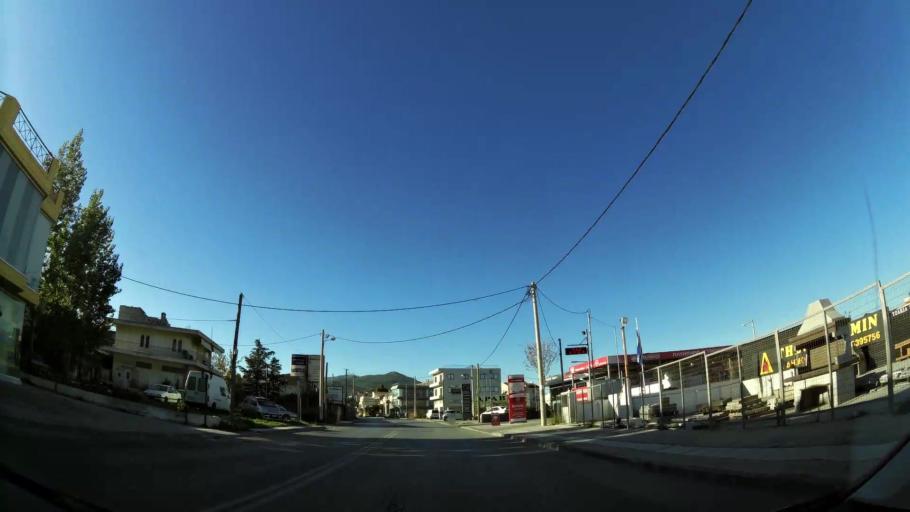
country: GR
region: Attica
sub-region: Nomarchia Anatolikis Attikis
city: Gerakas
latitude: 38.0206
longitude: 23.8466
